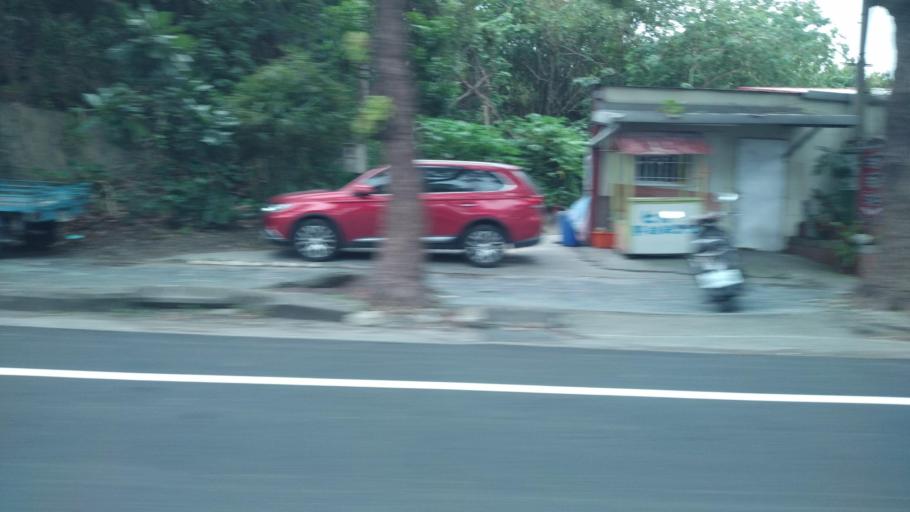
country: TW
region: Taiwan
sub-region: Hualien
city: Hualian
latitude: 24.0073
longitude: 121.6170
